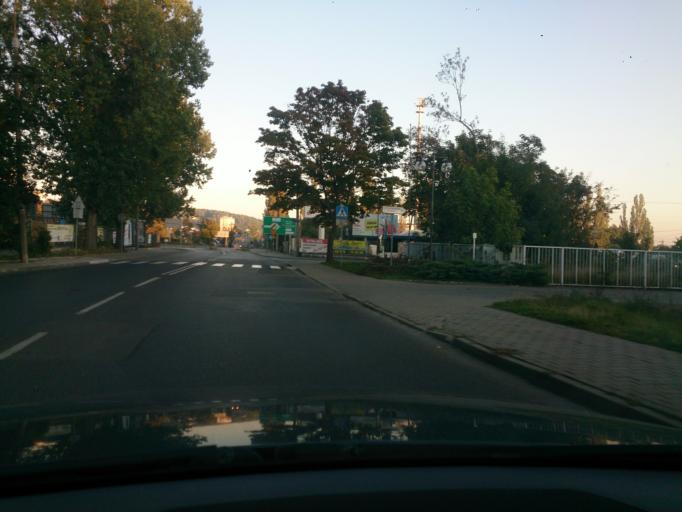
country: PL
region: Pomeranian Voivodeship
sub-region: Gdynia
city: Gdynia
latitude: 54.4918
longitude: 18.5331
